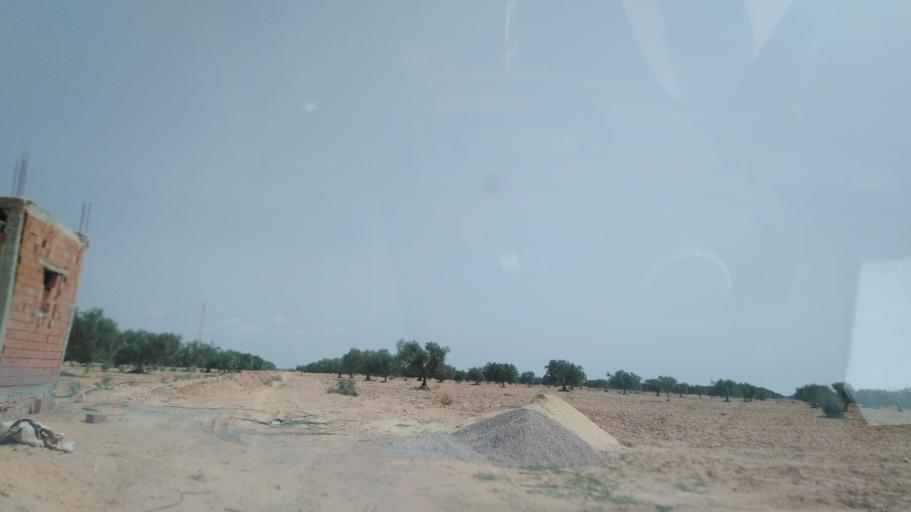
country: TN
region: Safaqis
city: Sfax
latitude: 34.6567
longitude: 10.5559
